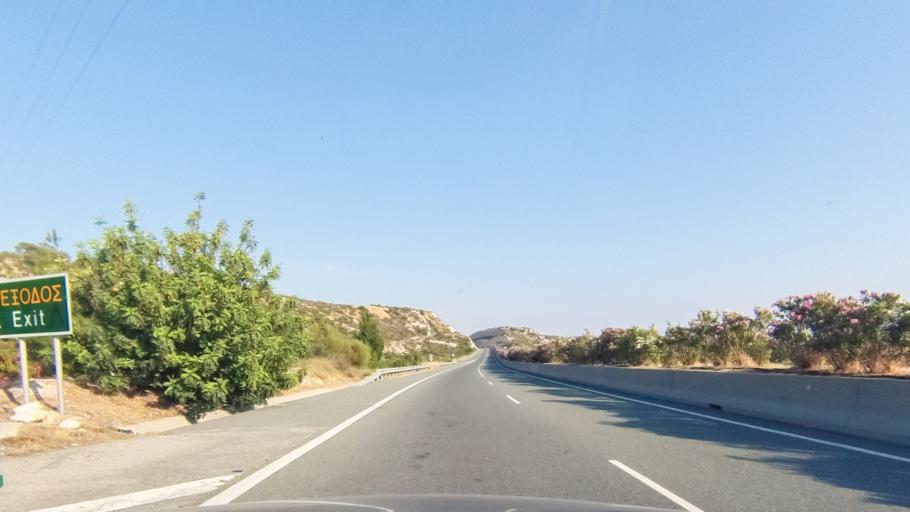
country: CY
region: Limassol
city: Sotira
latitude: 34.7003
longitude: 32.8593
